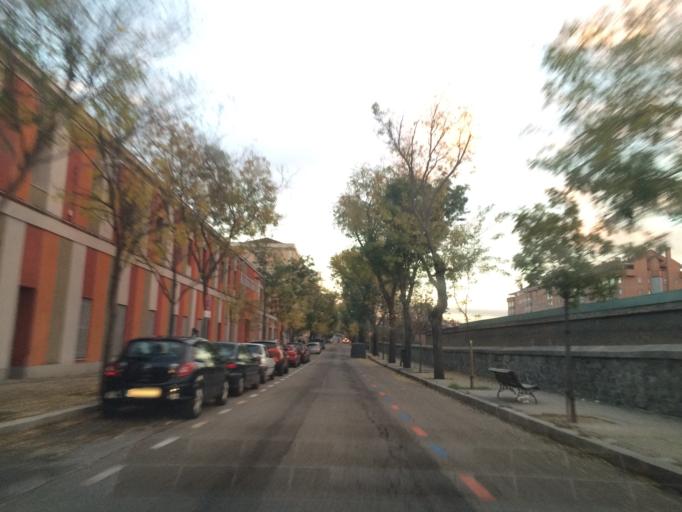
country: ES
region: Madrid
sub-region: Provincia de Madrid
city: Moncloa-Aravaca
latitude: 40.4258
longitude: -3.7235
